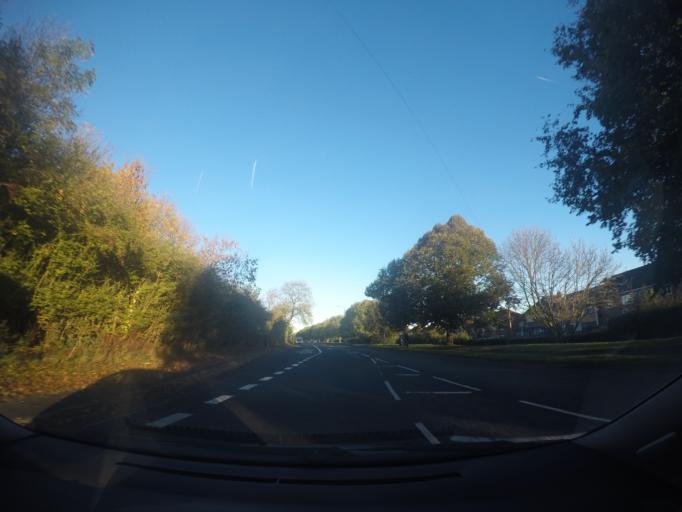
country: GB
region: England
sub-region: City of York
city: Skelton
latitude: 53.9834
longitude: -1.1186
